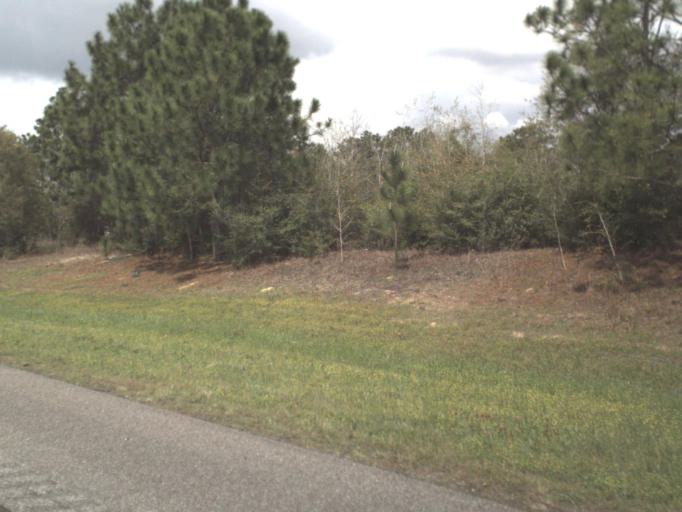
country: US
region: Florida
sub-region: Okaloosa County
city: Crestview
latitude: 30.6856
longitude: -86.7909
